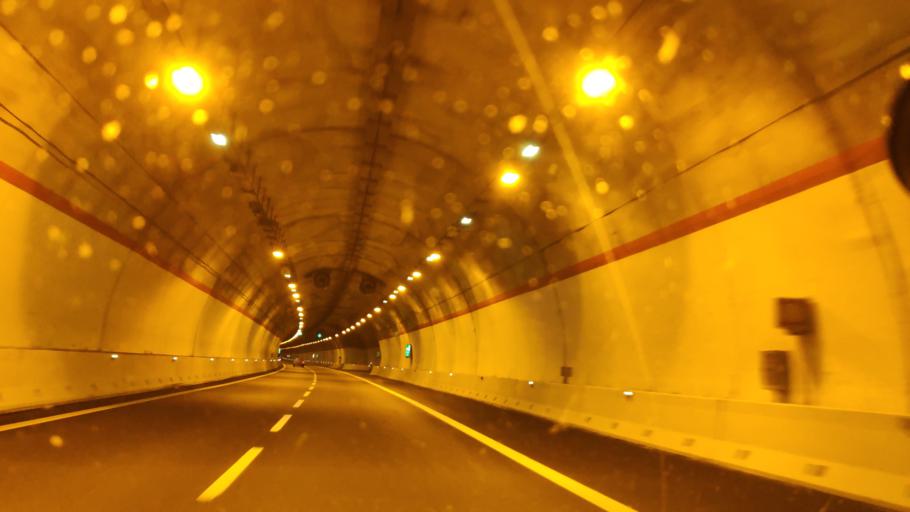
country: IT
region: Campania
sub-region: Provincia di Salerno
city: Casalbuono
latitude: 40.2123
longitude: 15.6737
